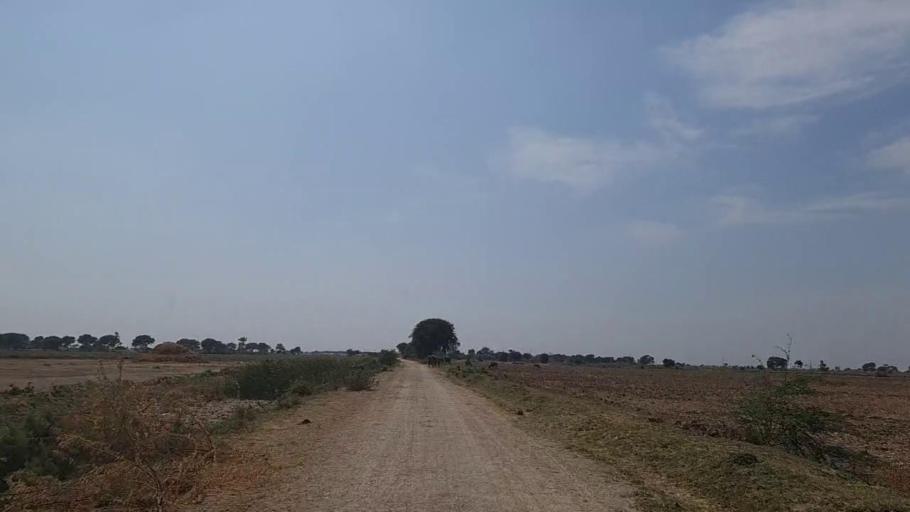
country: PK
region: Sindh
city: Jati
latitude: 24.5359
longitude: 68.3012
